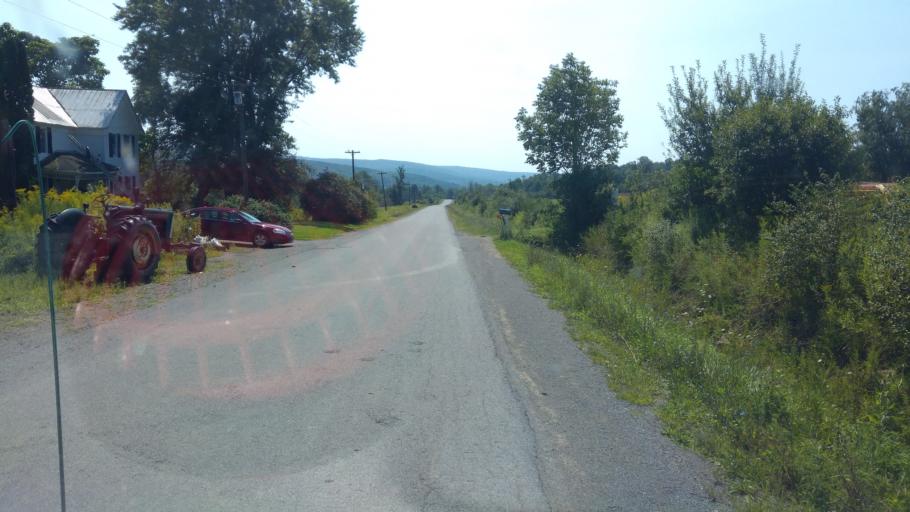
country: US
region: New York
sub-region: Allegany County
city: Belmont
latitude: 42.3391
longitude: -78.0408
